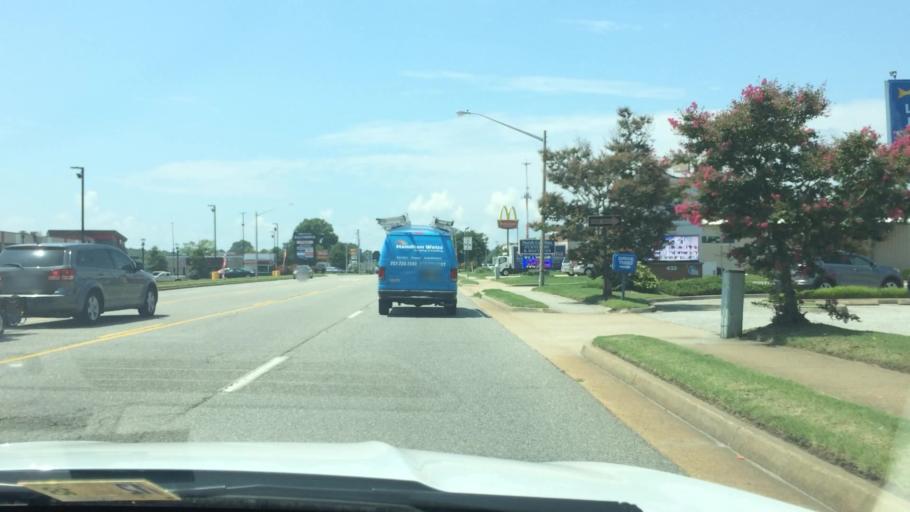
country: US
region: Virginia
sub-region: York County
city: Yorktown
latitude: 37.1307
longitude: -76.5340
